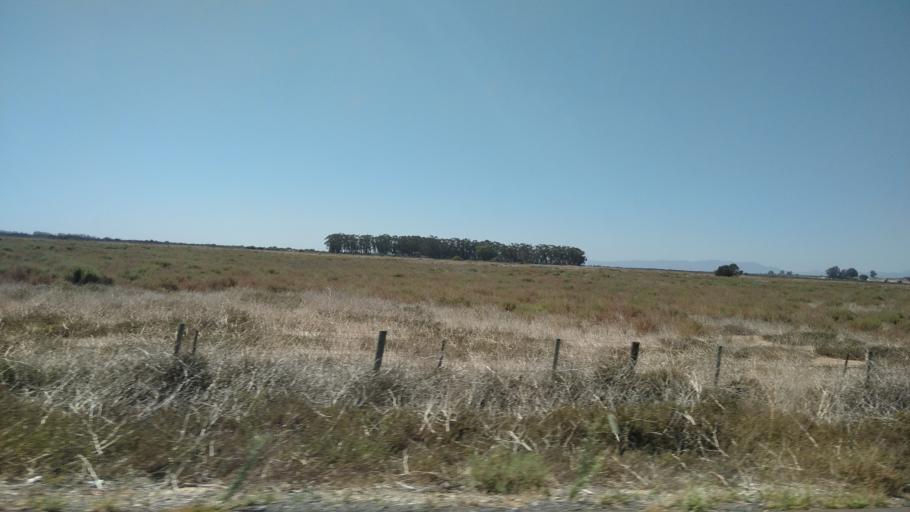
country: ZA
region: Western Cape
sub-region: West Coast District Municipality
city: Vredenburg
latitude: -32.9925
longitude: 18.1708
